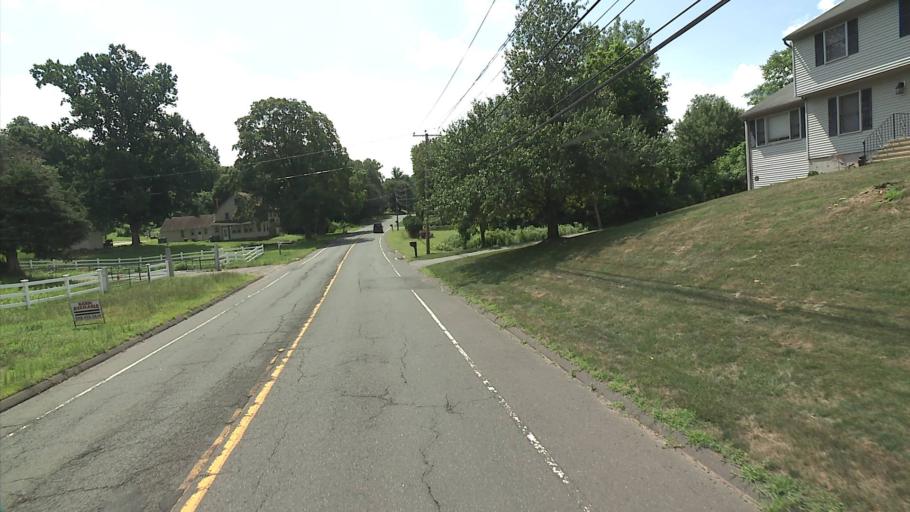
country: US
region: Connecticut
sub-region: Middlesex County
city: Cromwell
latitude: 41.6268
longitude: -72.6023
